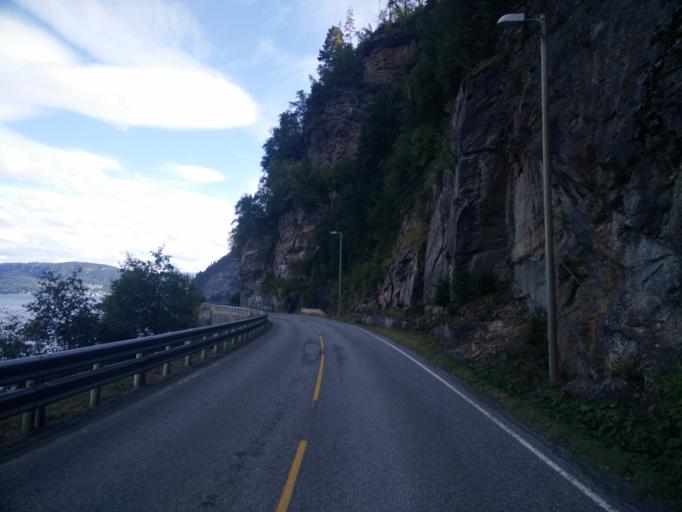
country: NO
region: Sor-Trondelag
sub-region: Skaun
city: Borsa
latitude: 63.3274
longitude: 10.1084
